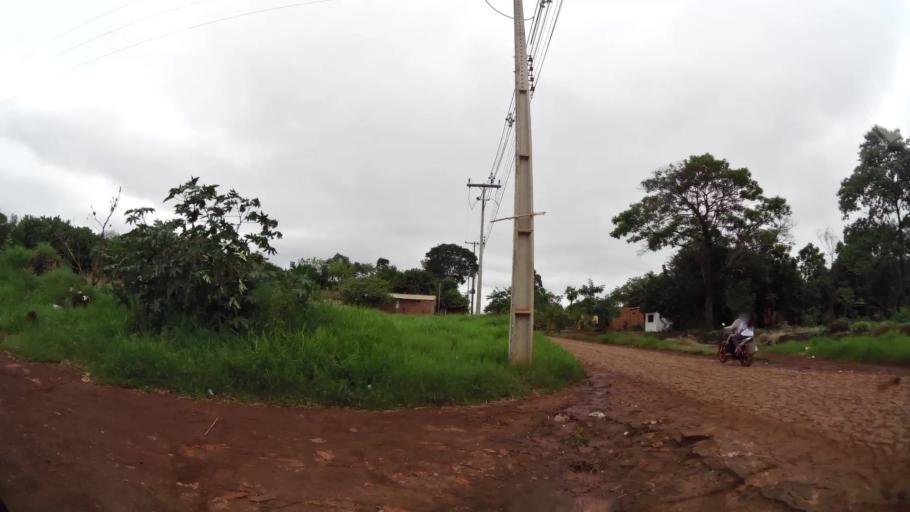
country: PY
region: Alto Parana
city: Presidente Franco
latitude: -25.5141
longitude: -54.6909
